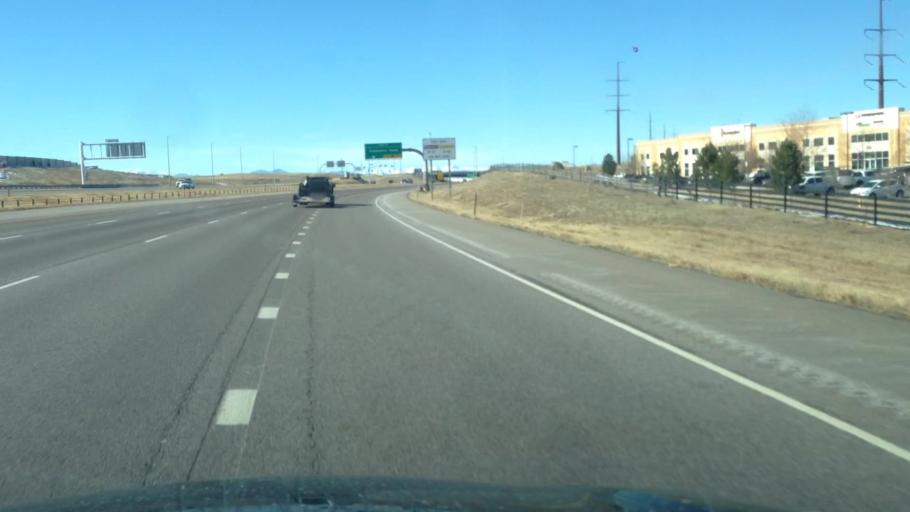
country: US
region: Colorado
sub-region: Douglas County
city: Stonegate
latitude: 39.5500
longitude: -104.8006
